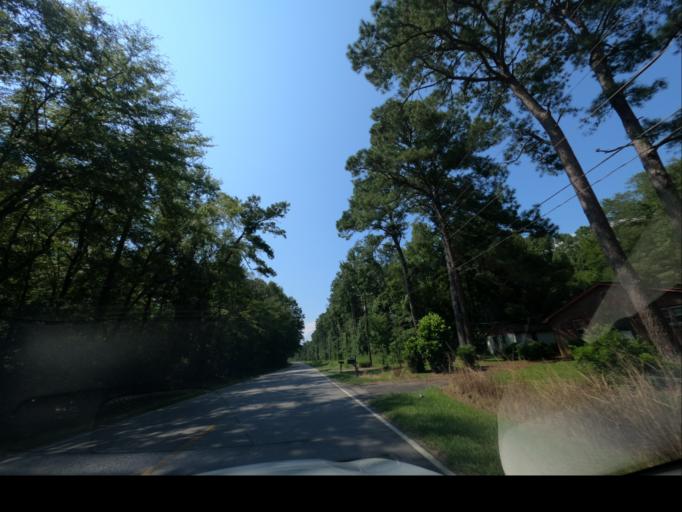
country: US
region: South Carolina
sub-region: Richland County
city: Hopkins
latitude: 33.8997
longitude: -80.9238
